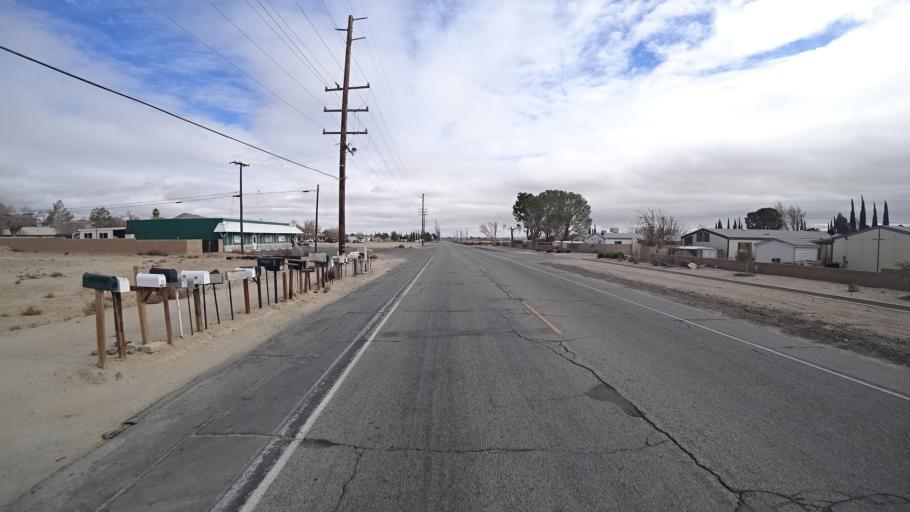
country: US
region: California
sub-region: Kern County
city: Rosamond
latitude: 34.8637
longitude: -118.2106
